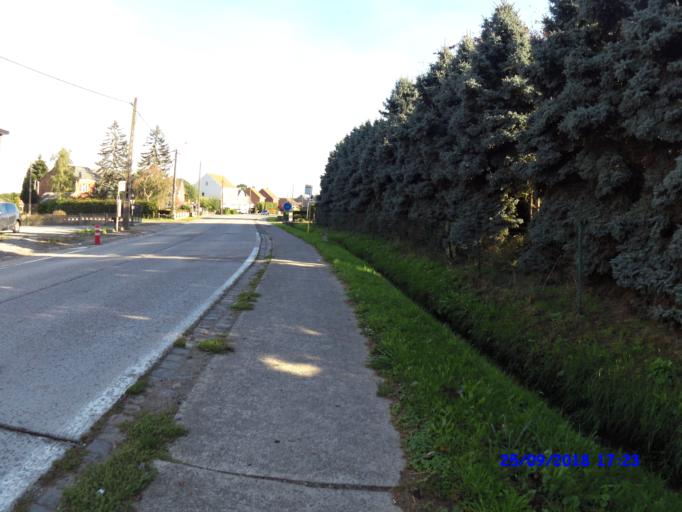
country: BE
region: Flanders
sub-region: Provincie Vlaams-Brabant
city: Aarschot
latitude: 51.0198
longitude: 4.8227
